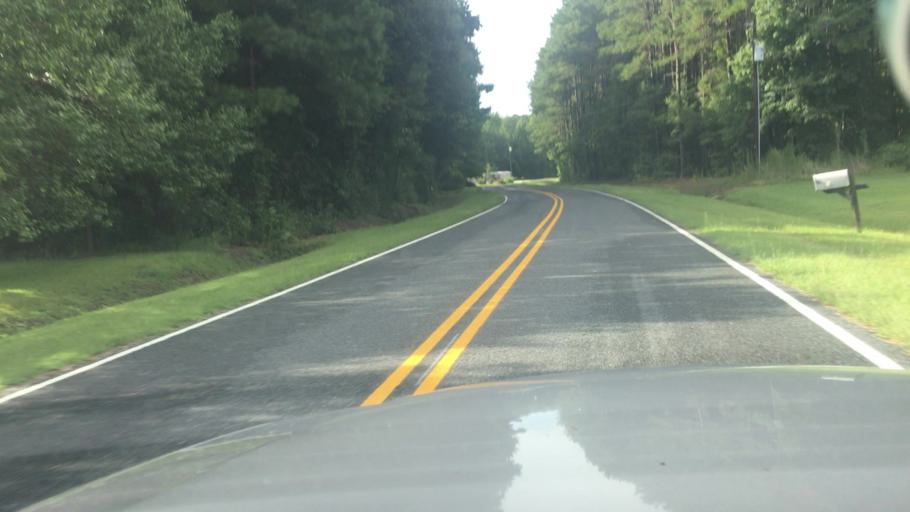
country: US
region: North Carolina
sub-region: Cumberland County
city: Eastover
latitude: 35.1584
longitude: -78.8534
